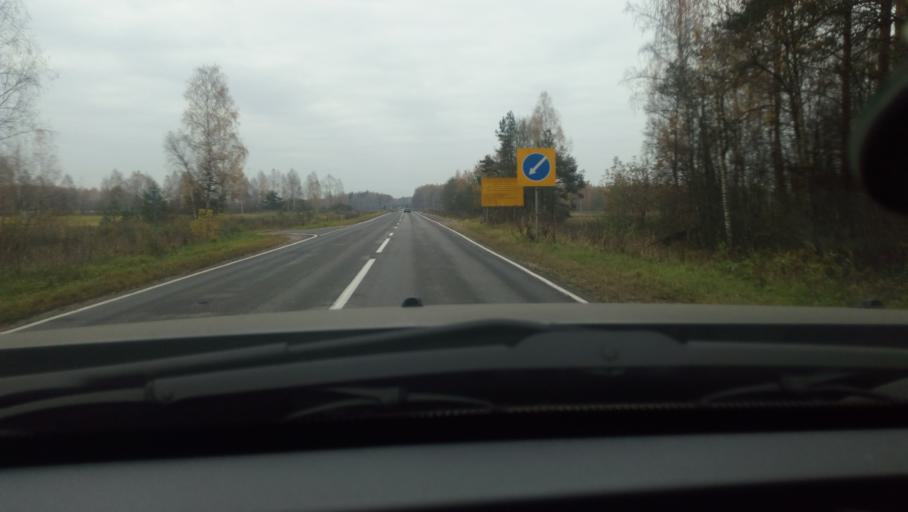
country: RU
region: Moskovskaya
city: Drezna
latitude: 55.7012
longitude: 38.8799
